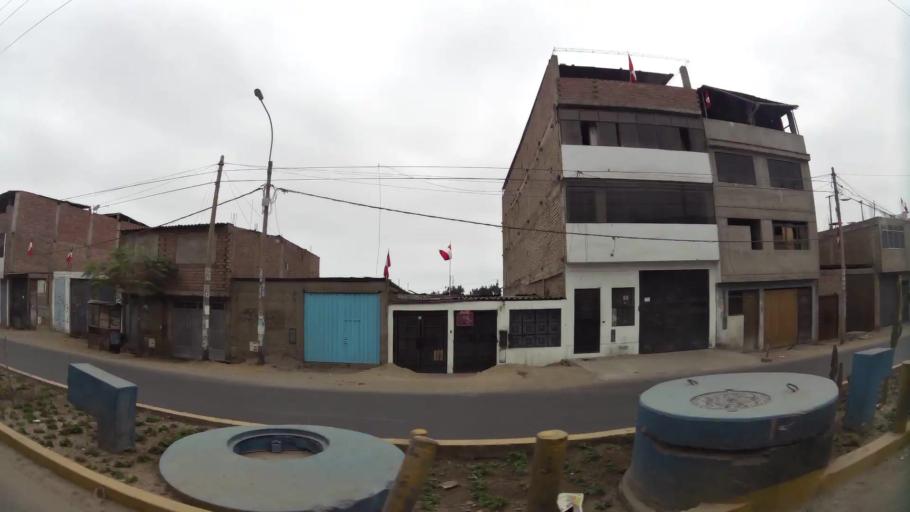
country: PE
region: Lima
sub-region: Lima
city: Surco
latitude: -12.1885
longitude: -76.9633
